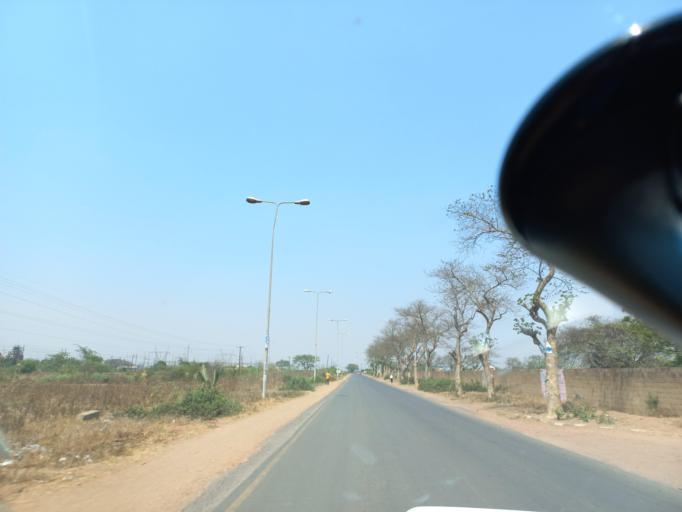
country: ZM
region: Lusaka
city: Kafue
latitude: -15.7479
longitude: 28.1653
